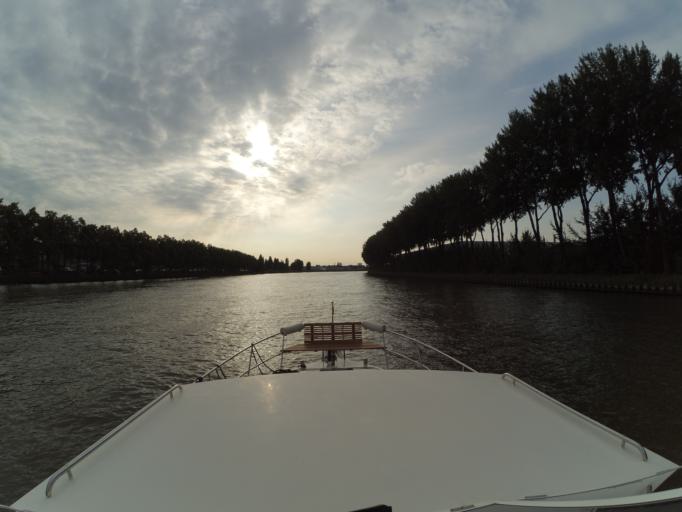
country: NL
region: Utrecht
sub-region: Stichtse Vecht
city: Maarssen
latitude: 52.1165
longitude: 5.0710
